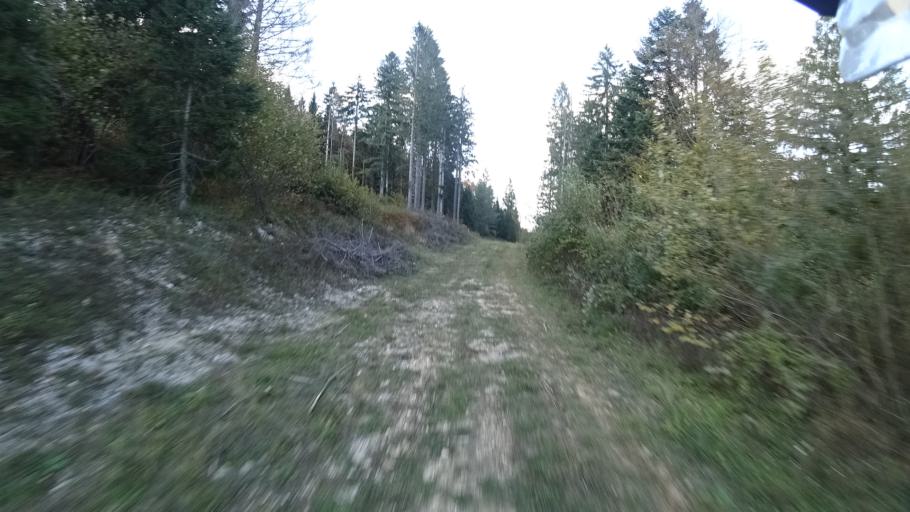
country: HR
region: Karlovacka
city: Plaski
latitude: 44.9859
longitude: 15.4168
